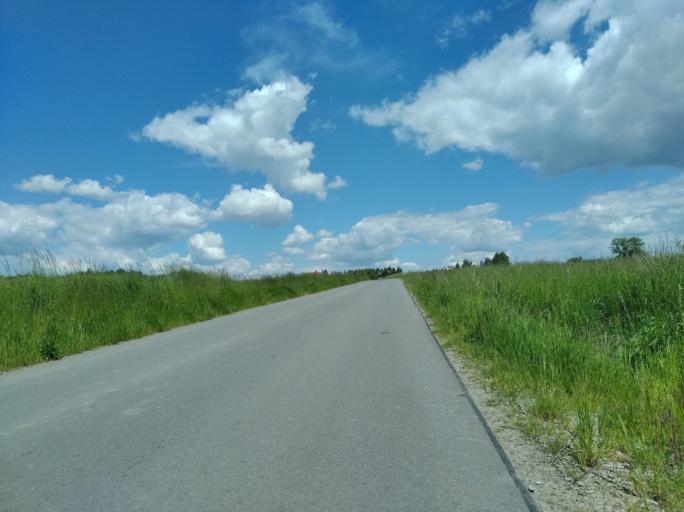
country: PL
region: Subcarpathian Voivodeship
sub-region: Powiat jasielski
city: Tarnowiec
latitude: 49.7717
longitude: 21.6114
